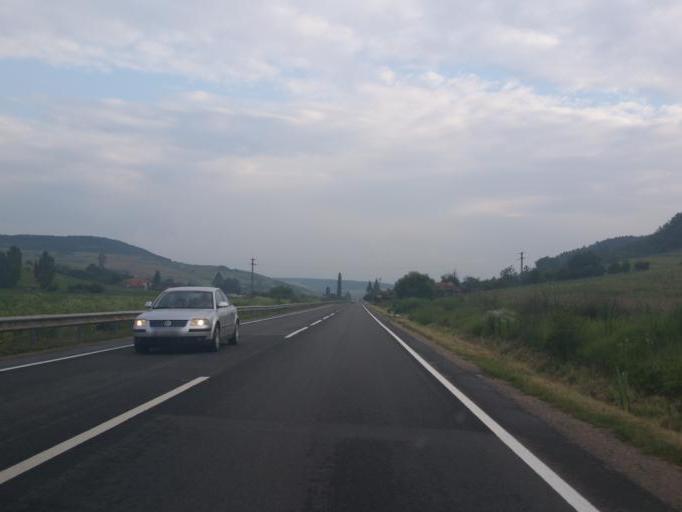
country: RO
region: Cluj
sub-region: Comuna Sanpaul
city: Sanpaul
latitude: 46.8803
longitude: 23.4200
